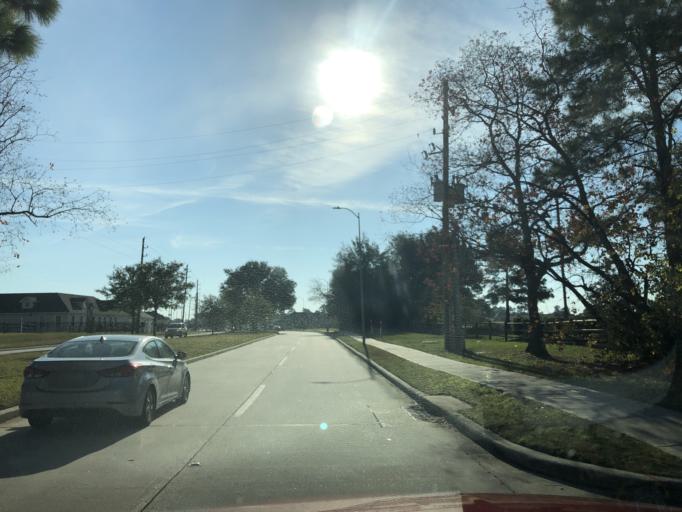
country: US
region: Texas
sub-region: Harris County
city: Tomball
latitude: 30.0359
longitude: -95.5598
